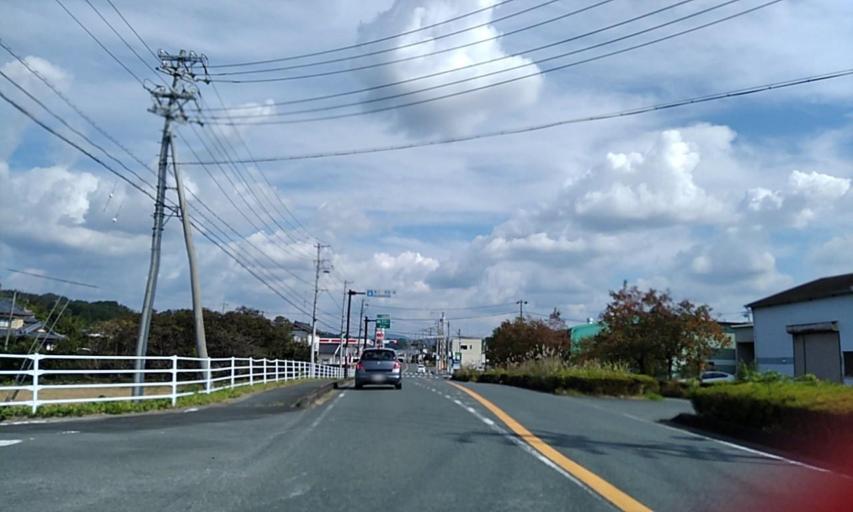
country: JP
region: Shizuoka
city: Mori
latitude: 34.8219
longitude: 137.8858
